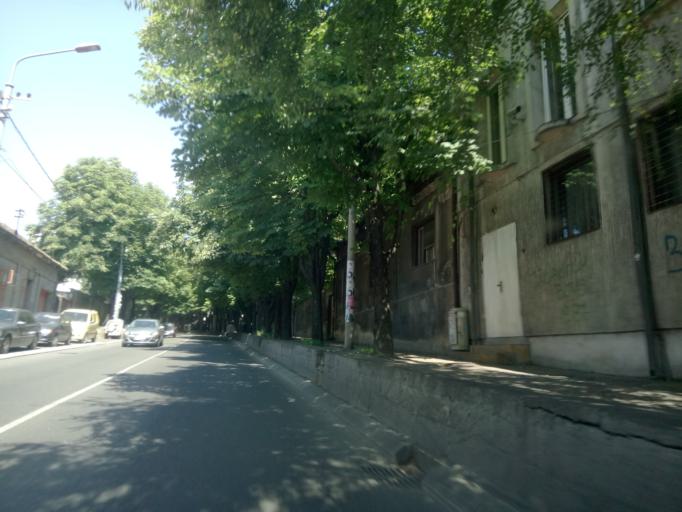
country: RS
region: Central Serbia
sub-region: Belgrade
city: Zemun
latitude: 44.8480
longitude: 20.4059
